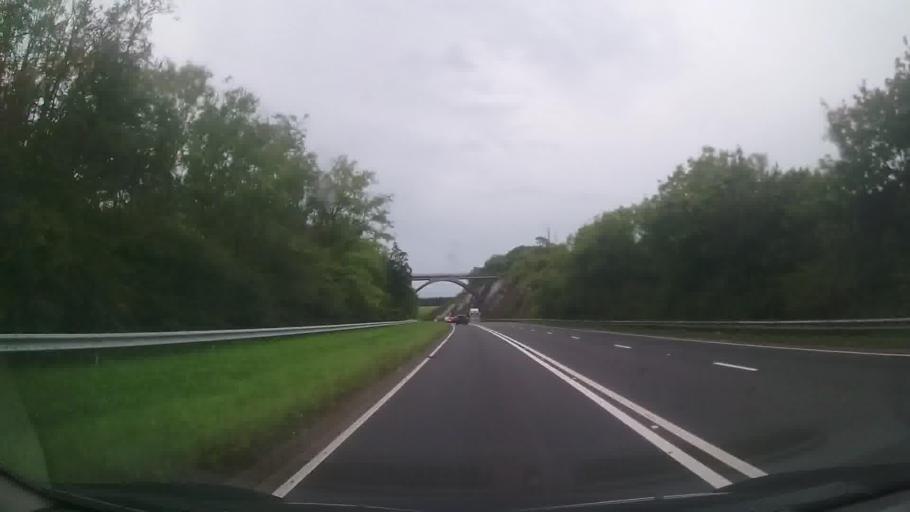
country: GB
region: Wales
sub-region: Pembrokeshire
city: Kilgetty
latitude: 51.7447
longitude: -4.6981
